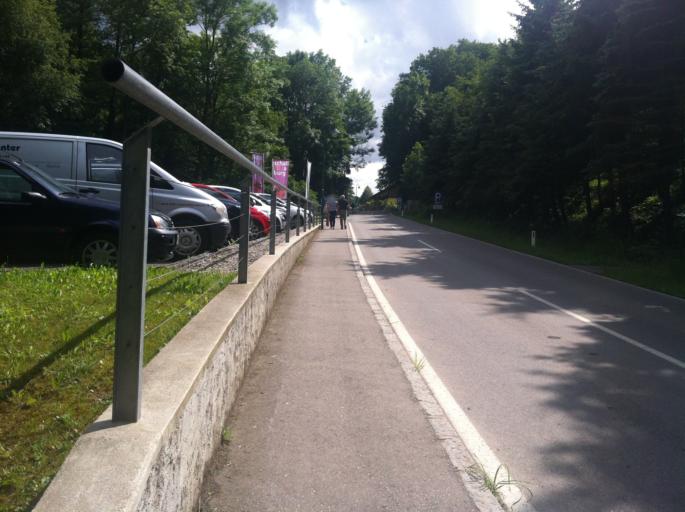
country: AT
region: Lower Austria
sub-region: Politischer Bezirk Melk
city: Loosdorf
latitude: 48.1865
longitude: 15.3558
